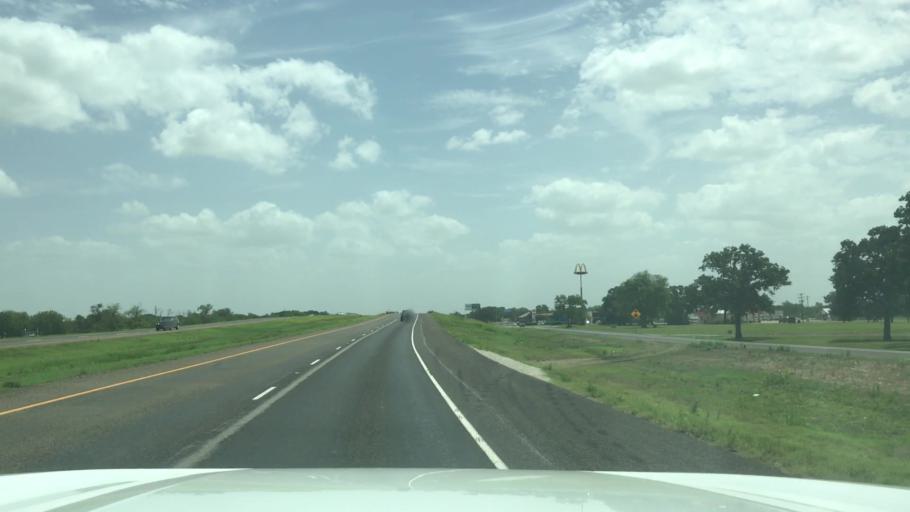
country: US
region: Texas
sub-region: Falls County
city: Marlin
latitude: 31.3097
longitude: -96.8748
